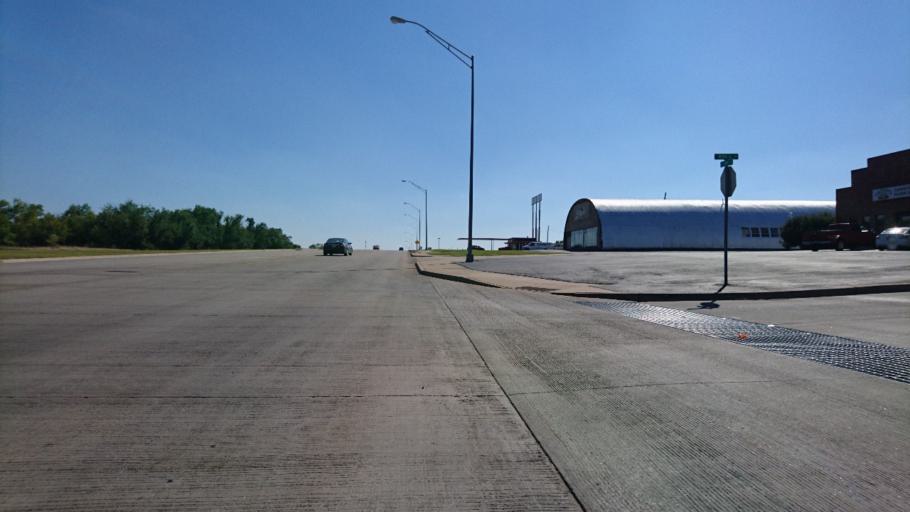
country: US
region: Oklahoma
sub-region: Custer County
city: Clinton
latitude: 35.5087
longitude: -98.9649
